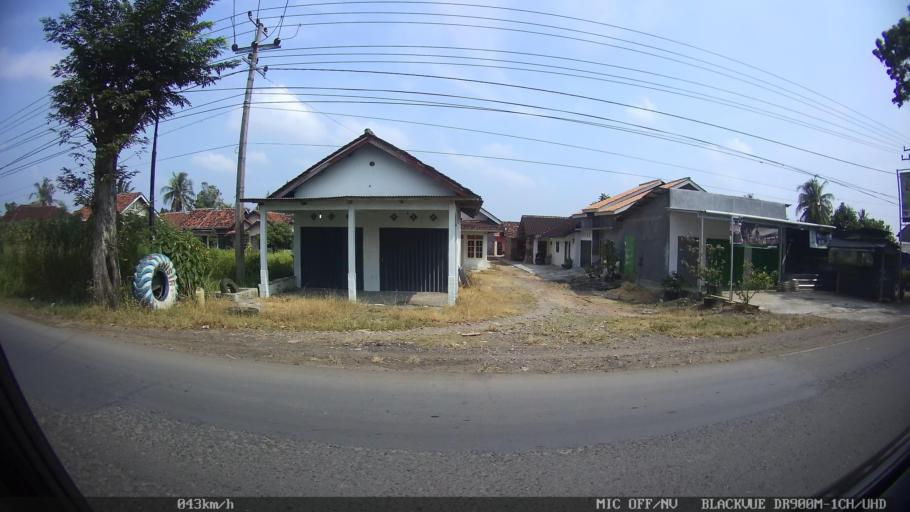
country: ID
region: Lampung
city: Gadingrejo
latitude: -5.3735
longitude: 105.0437
